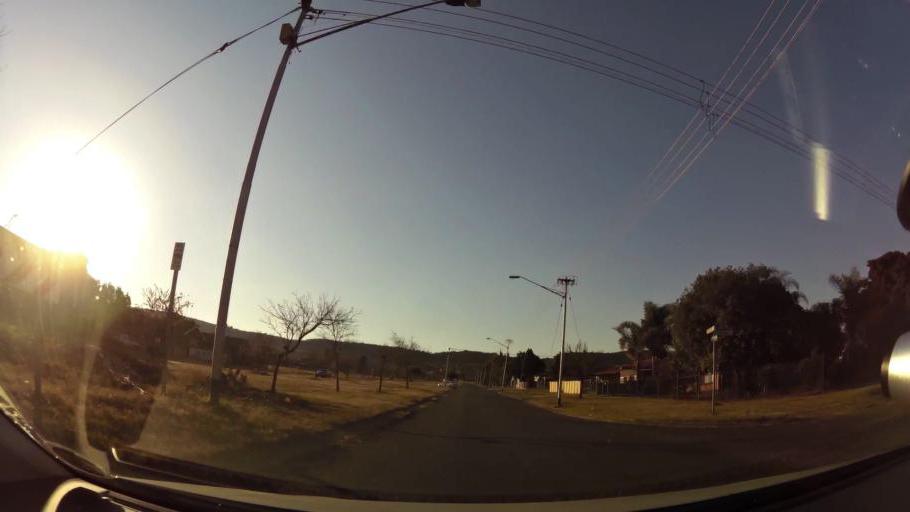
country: ZA
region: Gauteng
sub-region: City of Tshwane Metropolitan Municipality
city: Pretoria
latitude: -25.7393
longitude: 28.1174
